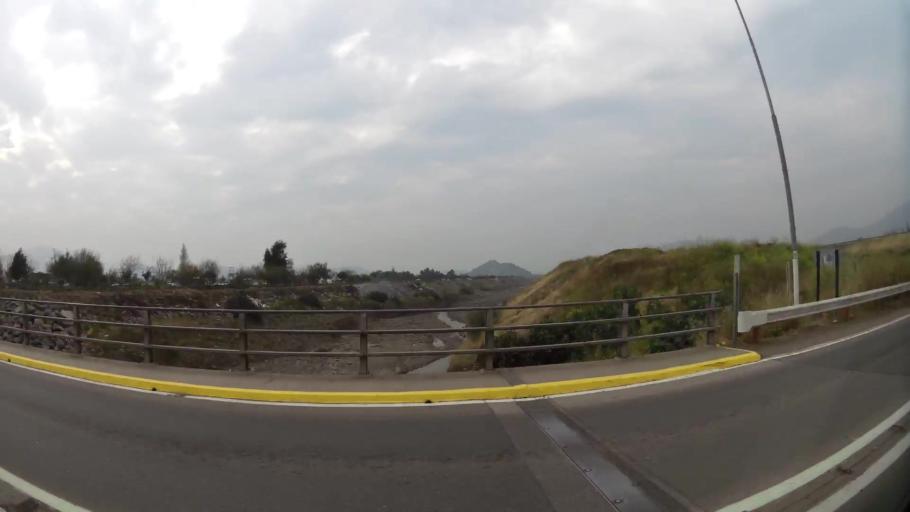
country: CL
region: Santiago Metropolitan
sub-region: Provincia de Chacabuco
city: Chicureo Abajo
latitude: -33.2073
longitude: -70.6685
